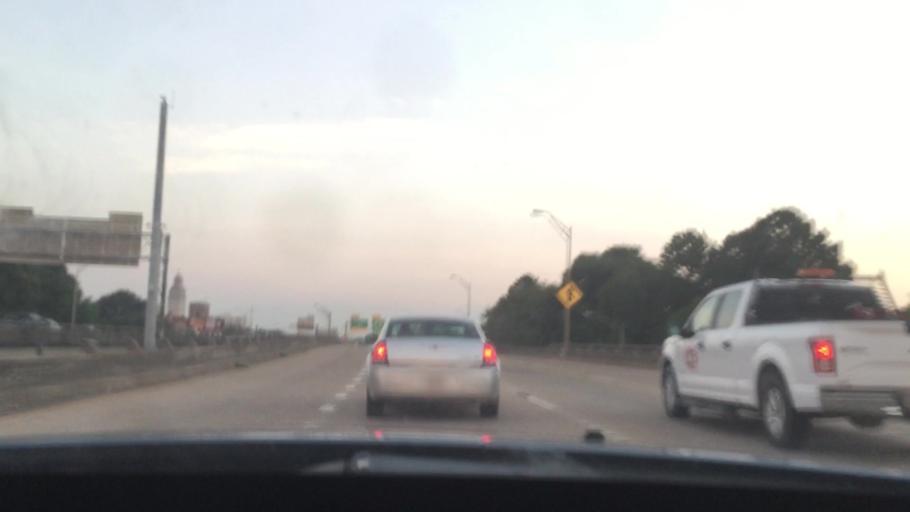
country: US
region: Louisiana
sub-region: East Baton Rouge Parish
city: Baton Rouge
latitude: 30.4435
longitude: -91.1785
